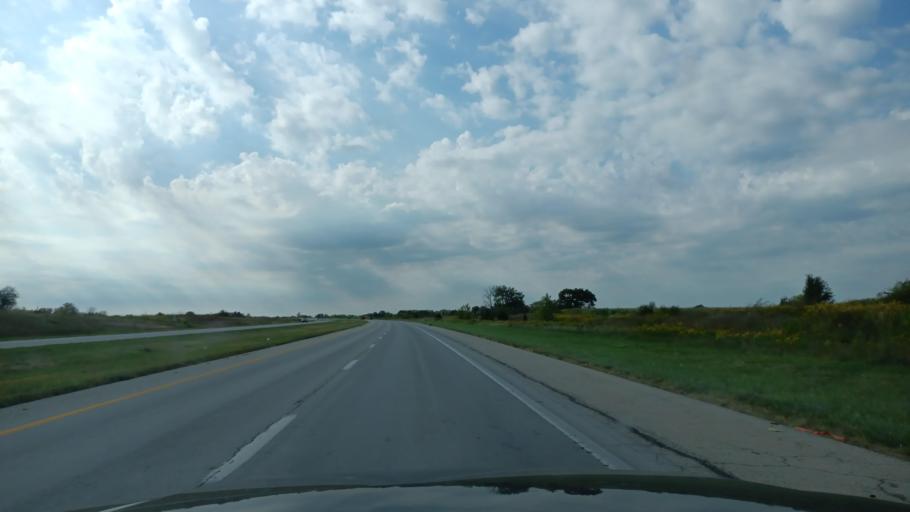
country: US
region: Ohio
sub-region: Fayette County
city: Washington Court House
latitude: 39.5136
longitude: -83.3615
